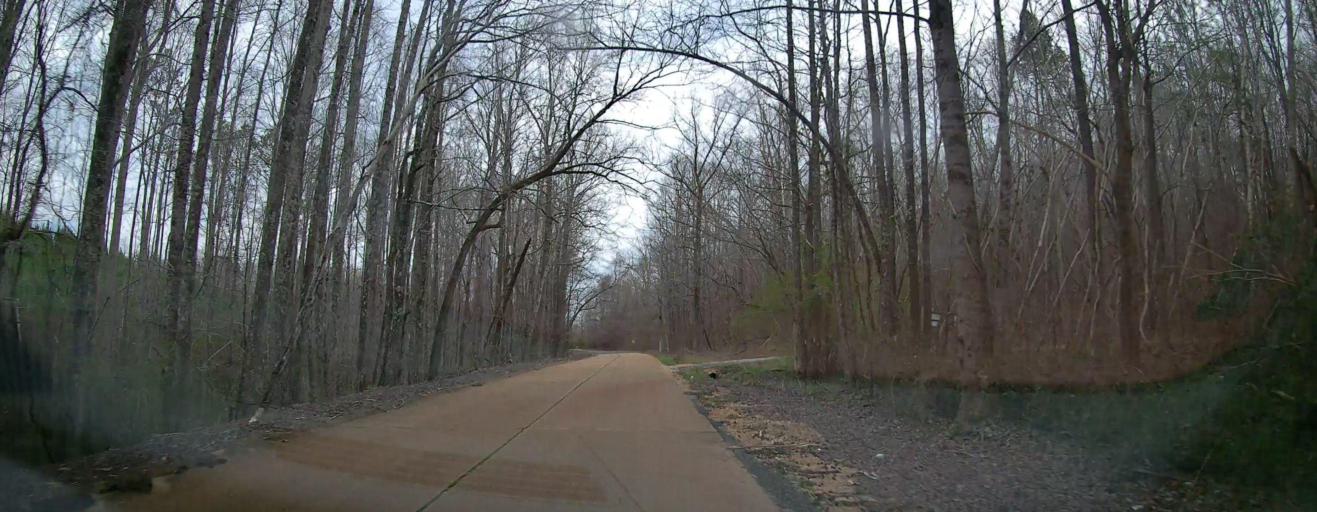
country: US
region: Alabama
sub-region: Marion County
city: Hamilton
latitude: 34.2035
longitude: -88.1911
